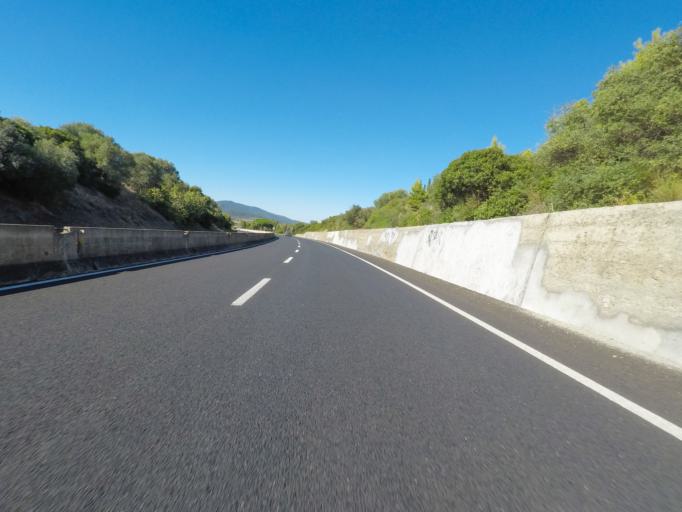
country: IT
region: Tuscany
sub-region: Provincia di Grosseto
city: Fonteblanda
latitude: 42.5671
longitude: 11.1723
